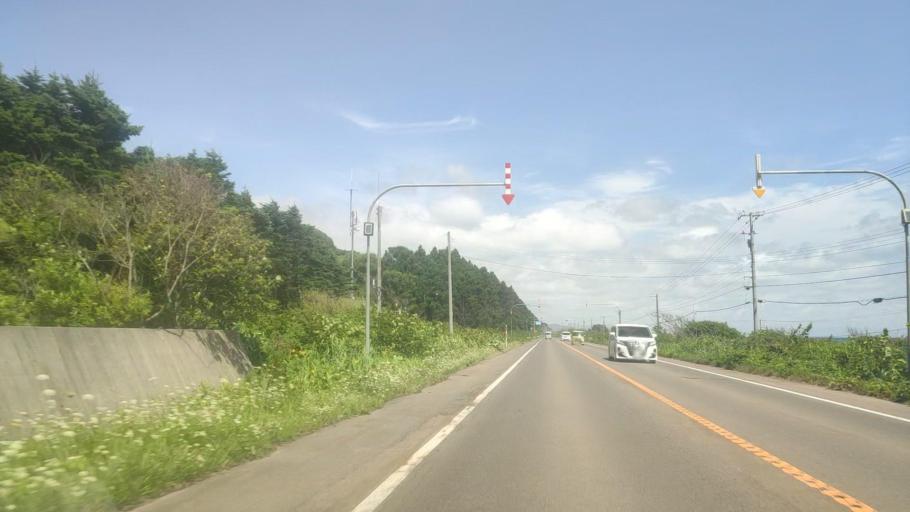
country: JP
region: Hokkaido
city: Niseko Town
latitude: 42.3369
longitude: 140.2796
